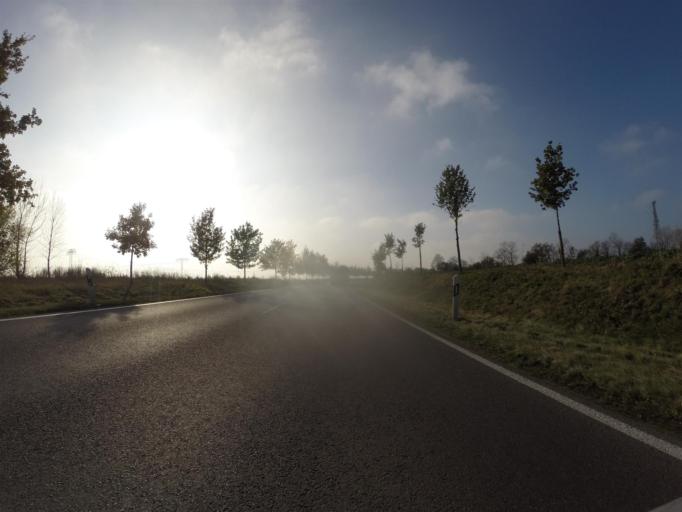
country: DE
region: Saxony
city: Markkleeberg
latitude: 51.2925
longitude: 12.3000
